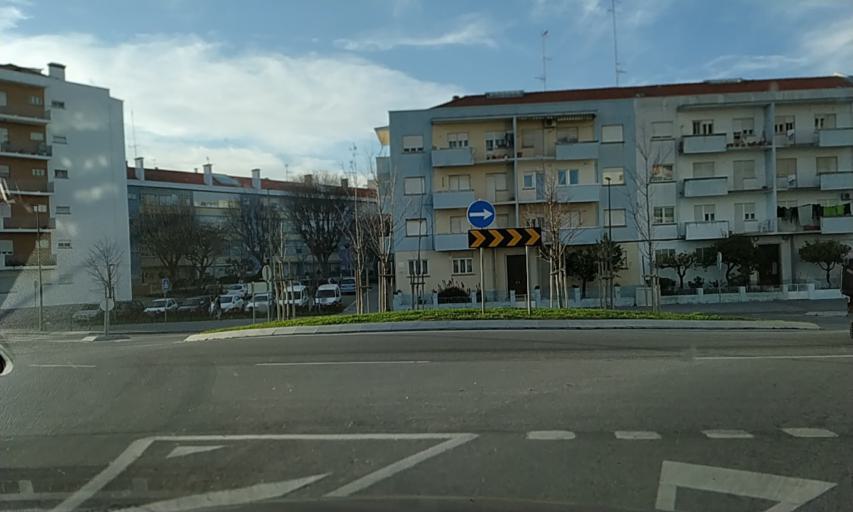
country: PT
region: Castelo Branco
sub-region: Castelo Branco
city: Castelo Branco
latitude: 39.8191
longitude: -7.4878
